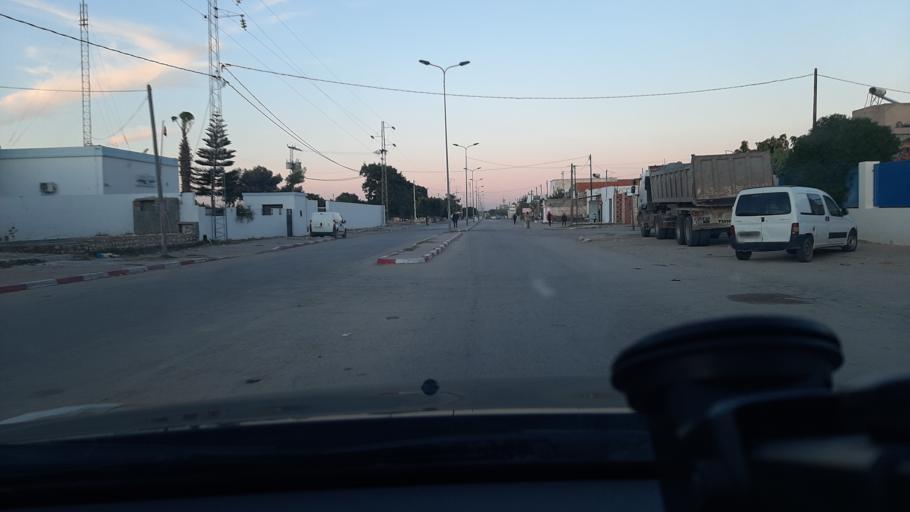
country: TN
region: Al Mahdiyah
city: Shurban
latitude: 34.9637
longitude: 10.3657
